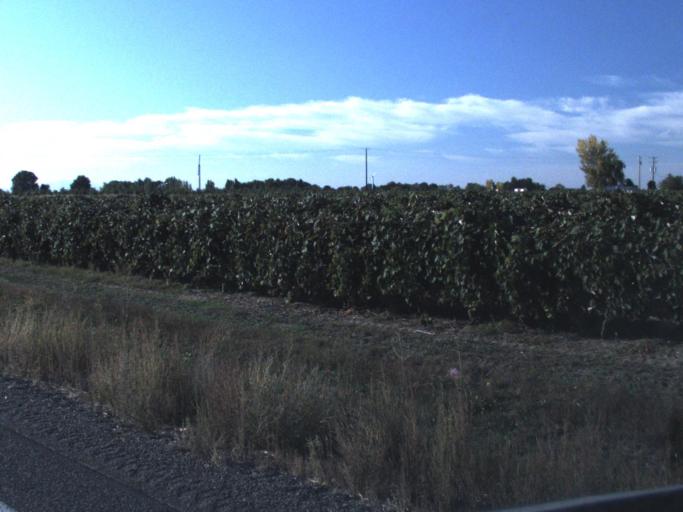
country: US
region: Washington
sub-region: Walla Walla County
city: Burbank
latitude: 46.2117
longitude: -118.9814
